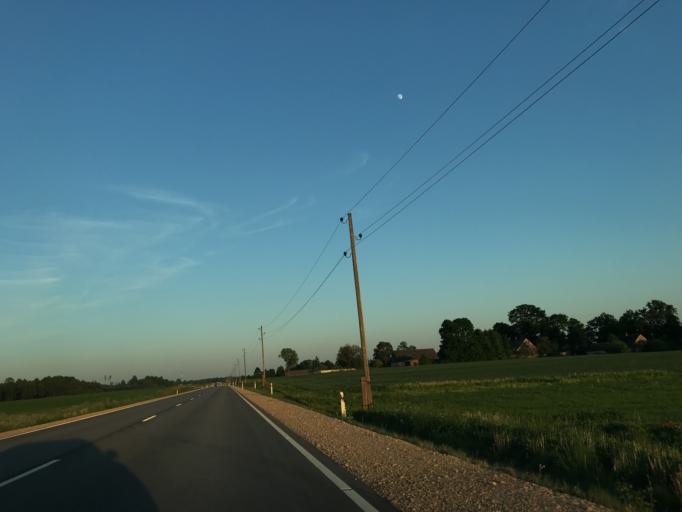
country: LV
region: Jaunjelgava
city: Jaunjelgava
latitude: 56.3865
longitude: 24.9748
